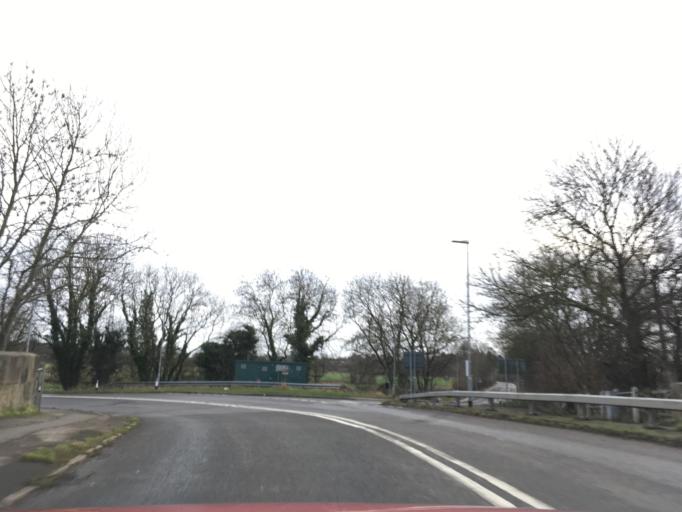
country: GB
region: England
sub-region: Leicestershire
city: Kegworth
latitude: 52.8400
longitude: -1.2684
